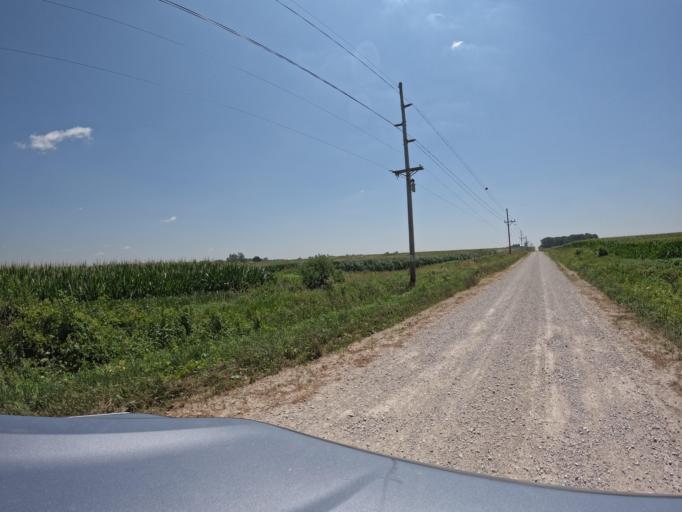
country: US
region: Iowa
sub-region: Keokuk County
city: Sigourney
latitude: 41.2898
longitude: -92.1808
